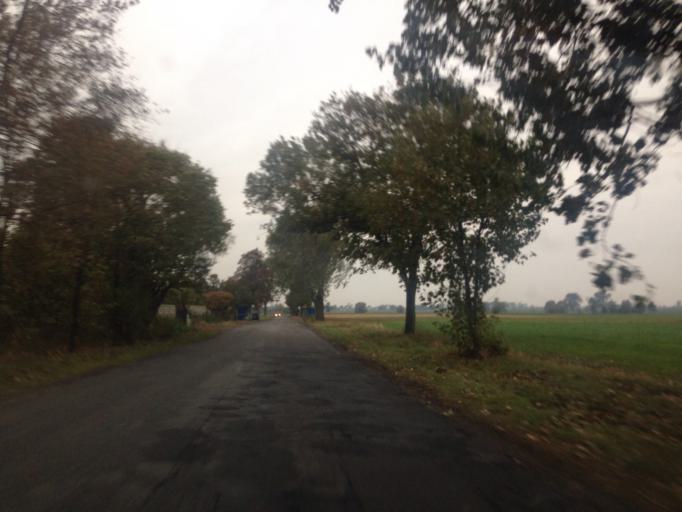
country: PL
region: Greater Poland Voivodeship
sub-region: Powiat poznanski
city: Kleszczewo
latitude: 52.3451
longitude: 17.1561
